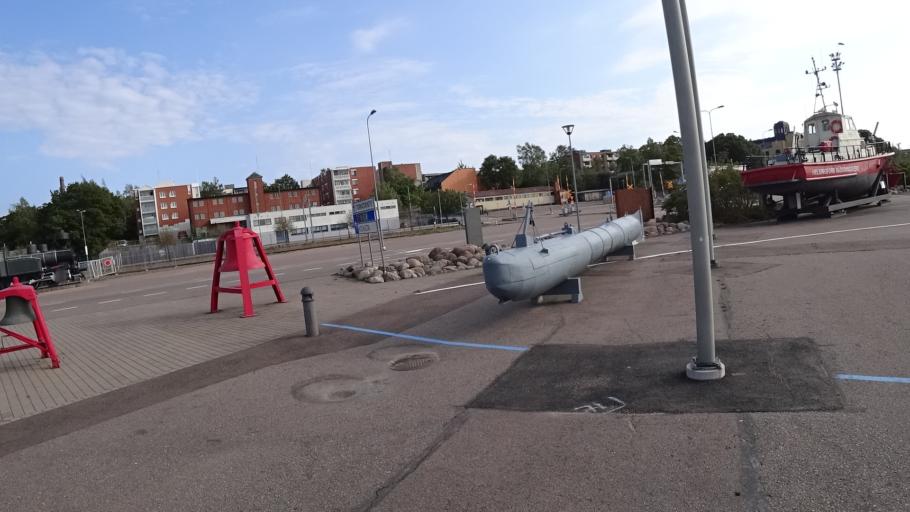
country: FI
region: Kymenlaakso
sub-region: Kotka-Hamina
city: Kotka
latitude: 60.4709
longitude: 26.9437
